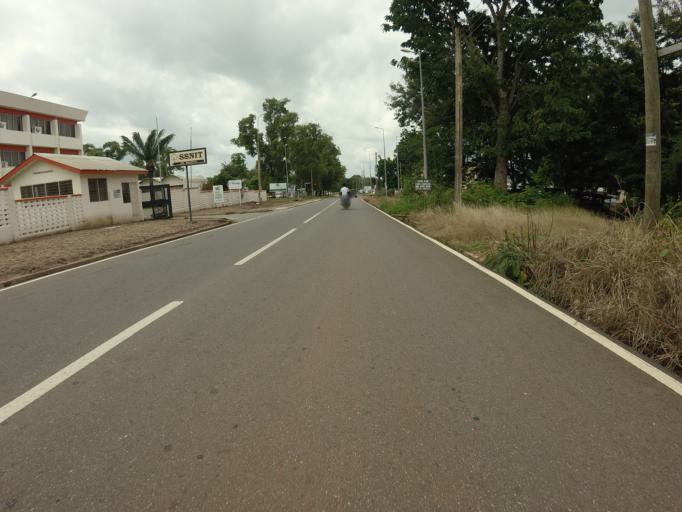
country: GH
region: Volta
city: Ho
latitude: 6.6081
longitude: 0.4646
